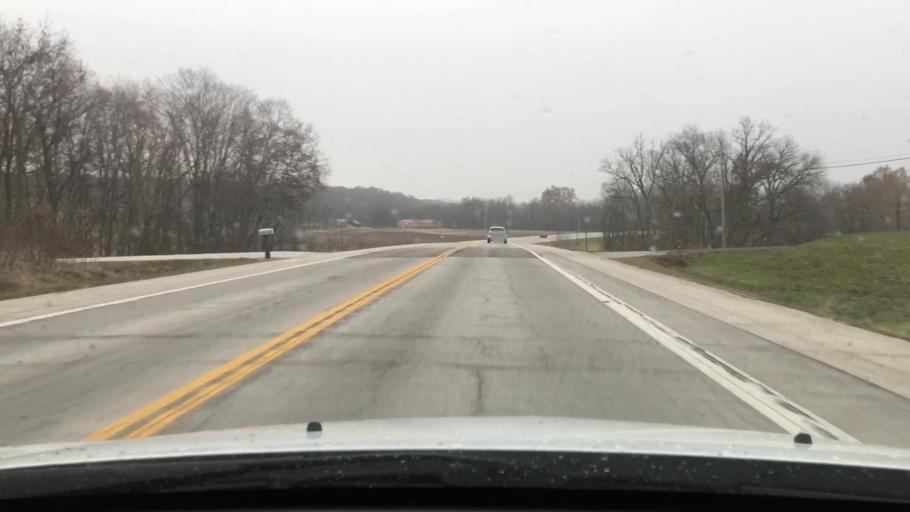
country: US
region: Missouri
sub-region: Pike County
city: Bowling Green
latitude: 39.3779
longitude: -91.1536
